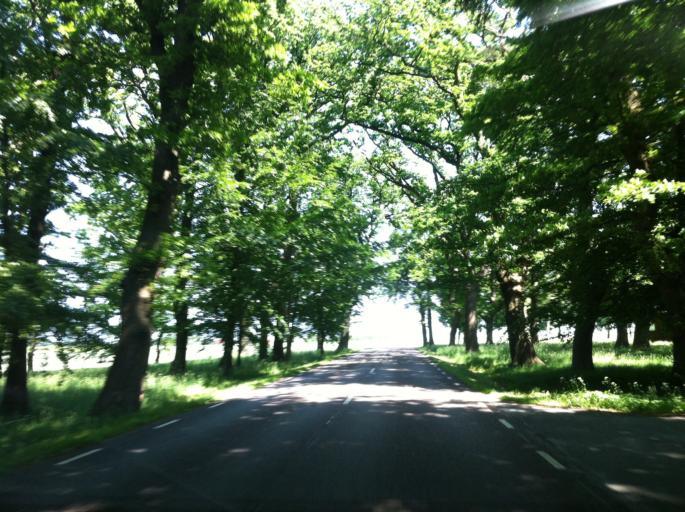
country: SE
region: Skane
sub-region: Helsingborg
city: Barslov
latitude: 55.9779
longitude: 12.8586
